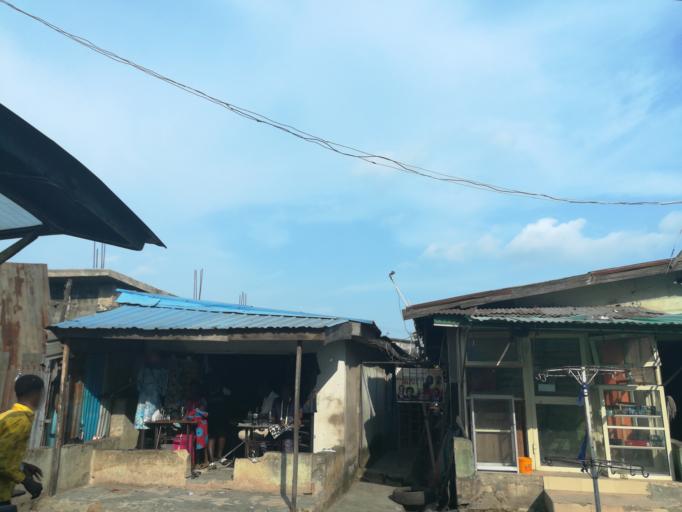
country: NG
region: Lagos
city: Ojota
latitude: 6.5937
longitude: 3.4006
